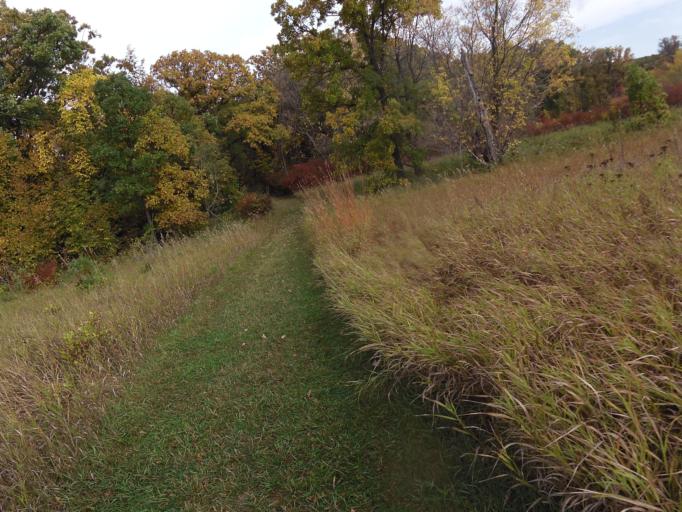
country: US
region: North Dakota
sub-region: Pembina County
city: Cavalier
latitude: 48.7781
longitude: -97.7311
